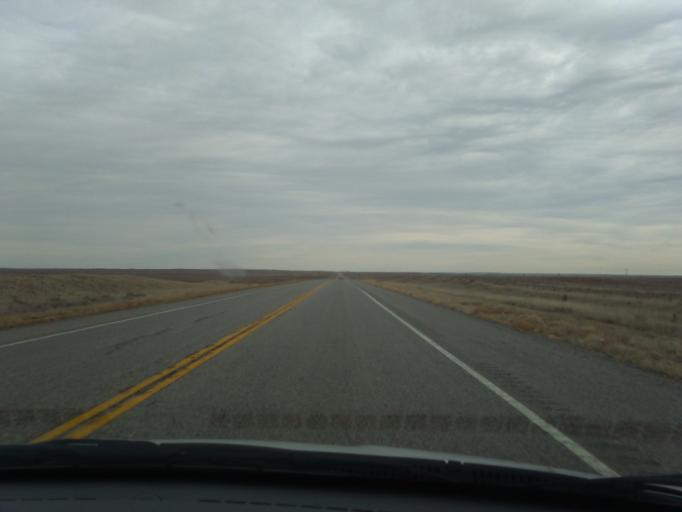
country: US
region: Colorado
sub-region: Morgan County
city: Brush
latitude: 40.2512
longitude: -103.4950
